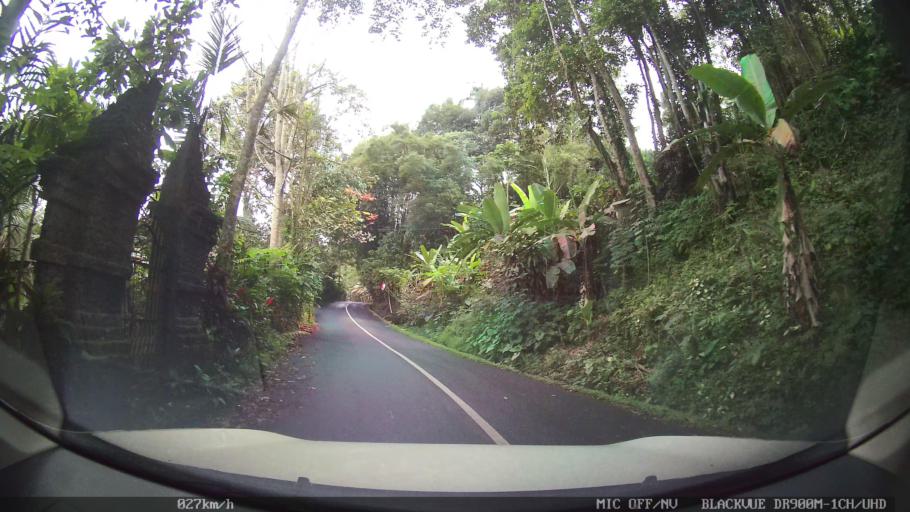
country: ID
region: Bali
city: Peneng
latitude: -8.3619
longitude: 115.1794
